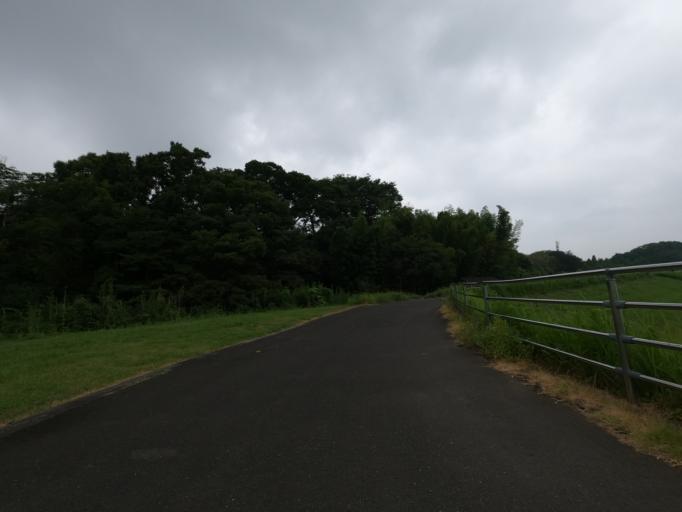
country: JP
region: Ibaraki
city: Toride
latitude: 35.9289
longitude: 140.0482
